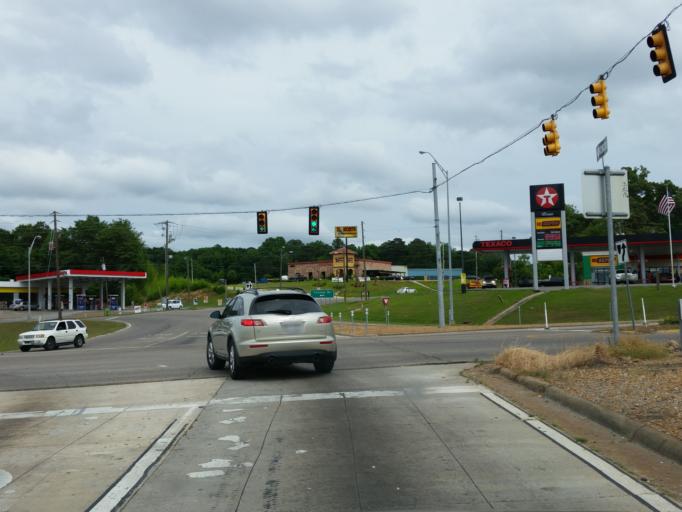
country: US
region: Mississippi
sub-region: Lauderdale County
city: Meridian
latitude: 32.3519
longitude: -88.6914
